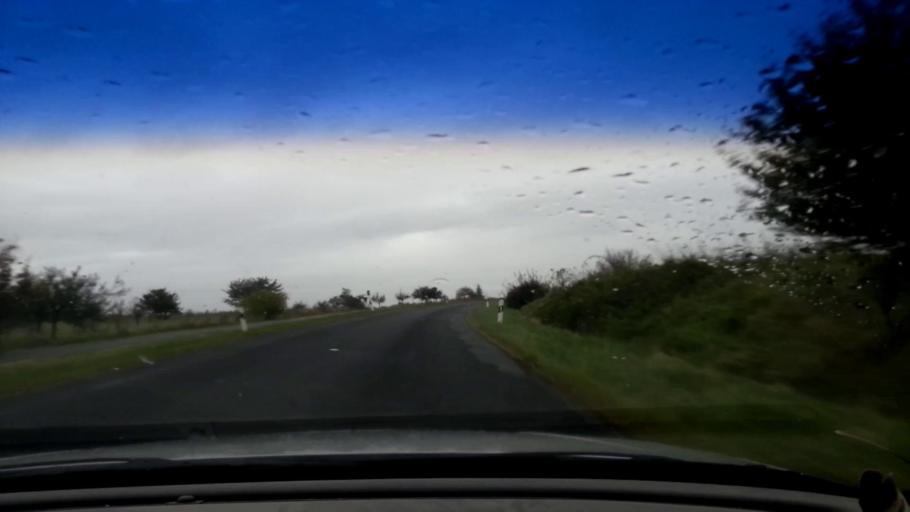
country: DE
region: Bavaria
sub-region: Upper Franconia
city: Priesendorf
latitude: 49.8750
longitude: 10.7099
